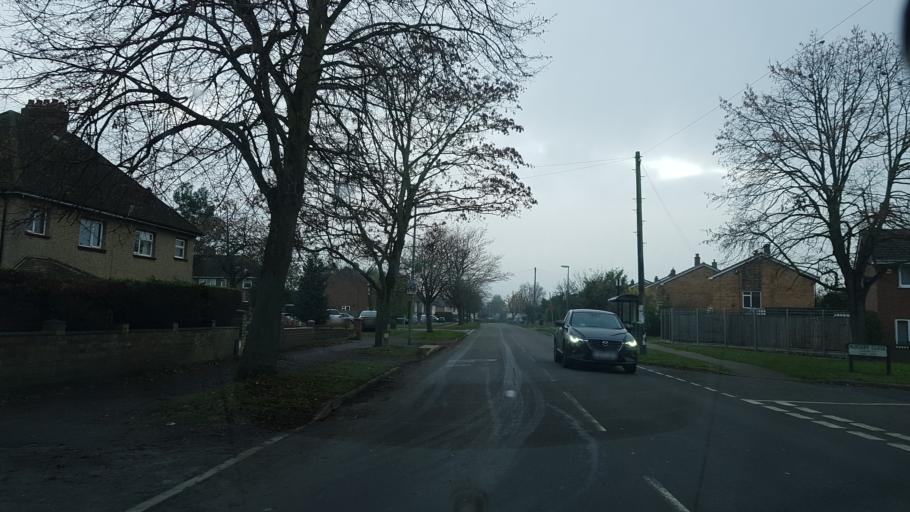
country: GB
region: England
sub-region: Central Bedfordshire
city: Biggleswade
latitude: 52.0953
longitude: -0.2518
